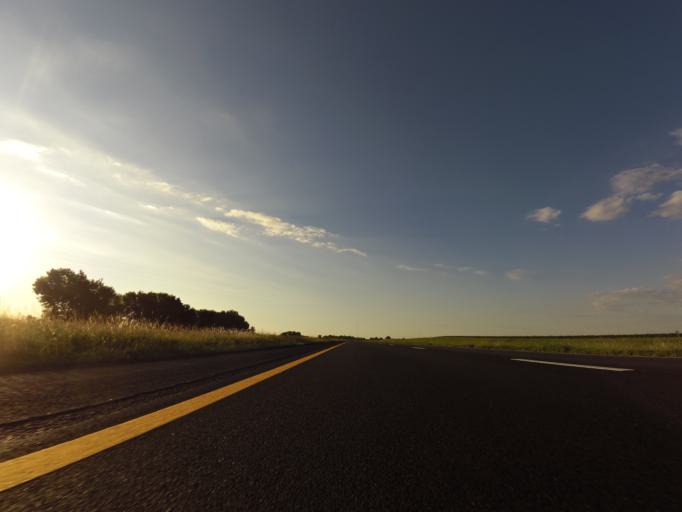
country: US
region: Kansas
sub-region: Sedgwick County
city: Colwich
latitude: 37.8349
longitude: -97.5673
